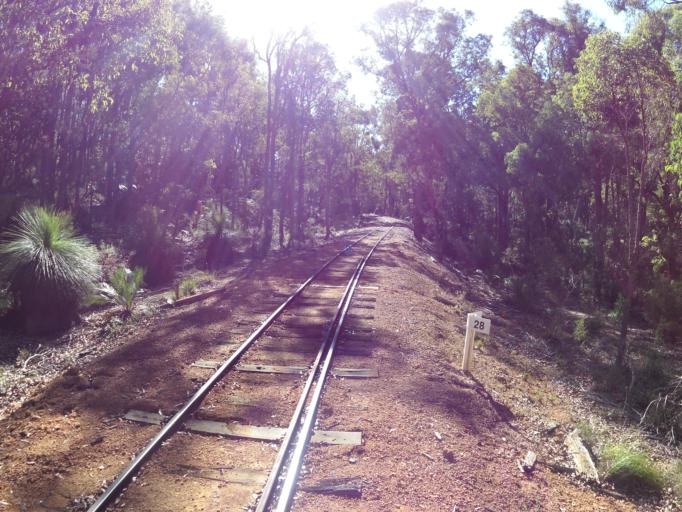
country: AU
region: Western Australia
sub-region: Waroona
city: Waroona
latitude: -32.7199
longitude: 116.1011
